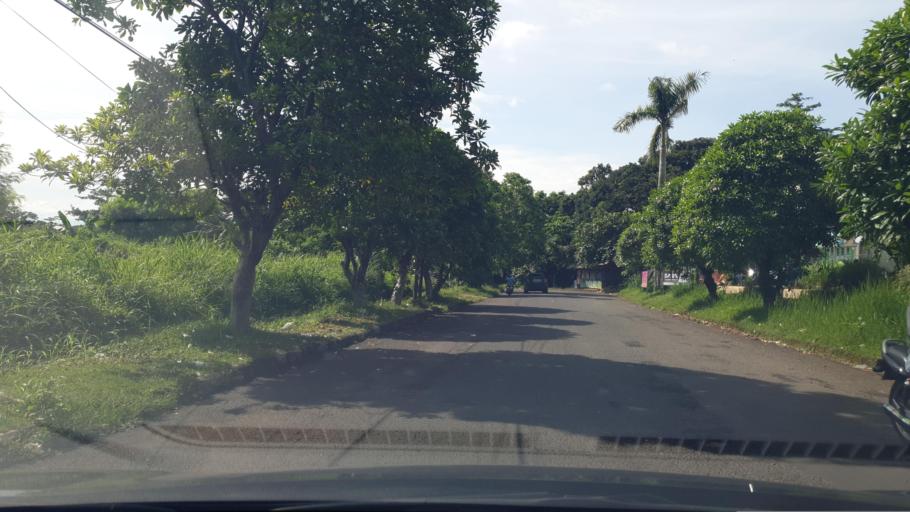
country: ID
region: West Java
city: Sawangan
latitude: -6.4037
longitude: 106.7726
